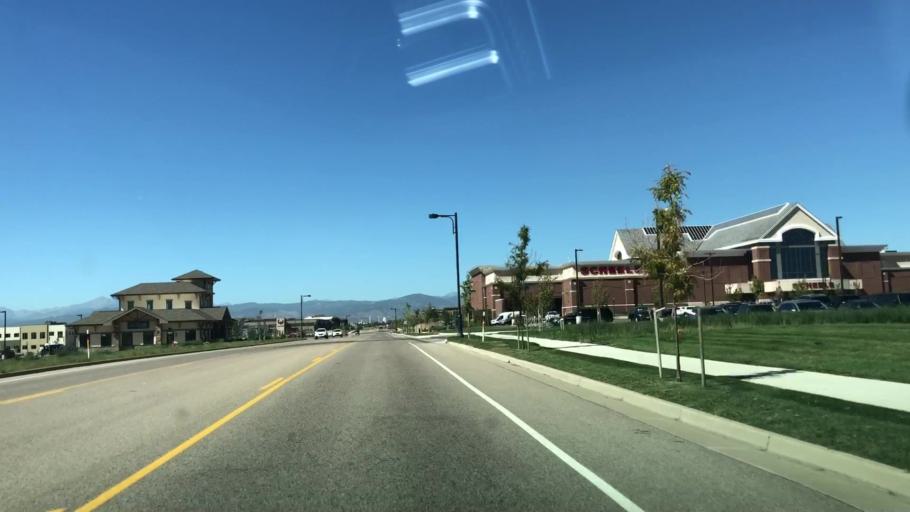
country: US
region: Colorado
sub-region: Weld County
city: Johnstown
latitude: 40.4036
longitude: -104.9766
